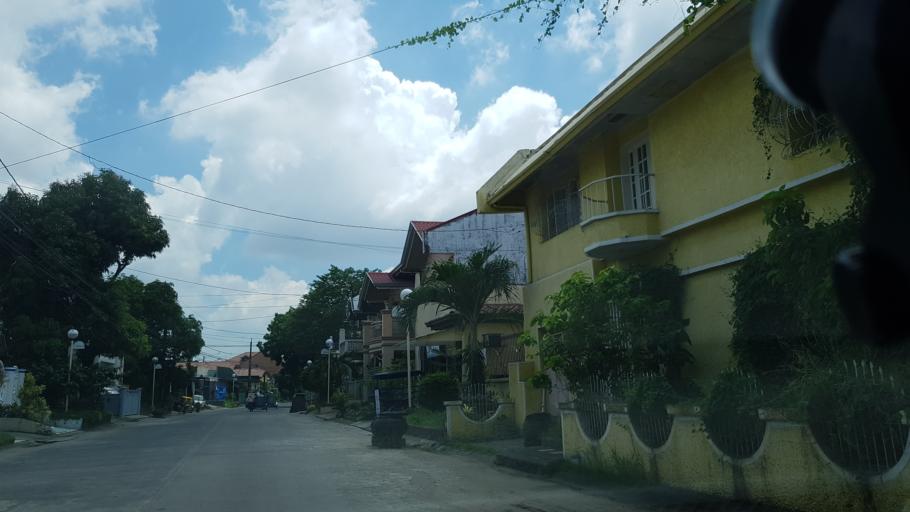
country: PH
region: Calabarzon
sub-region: Province of Rizal
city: Las Pinas
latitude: 14.4350
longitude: 120.9825
